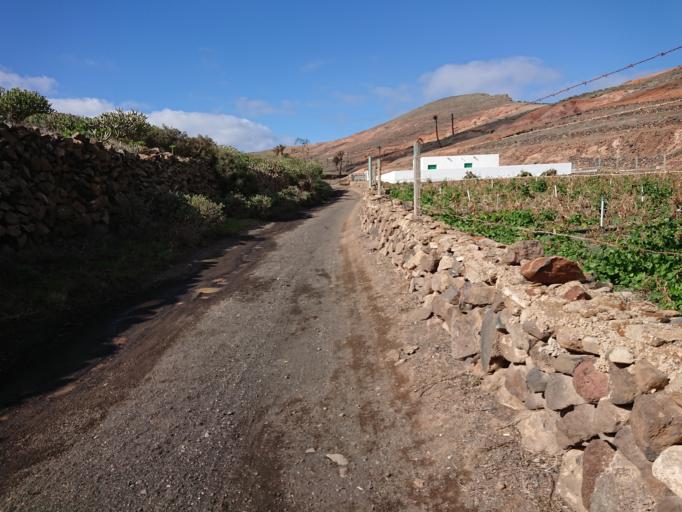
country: ES
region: Canary Islands
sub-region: Provincia de Las Palmas
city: Haria
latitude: 29.1446
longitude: -13.5107
